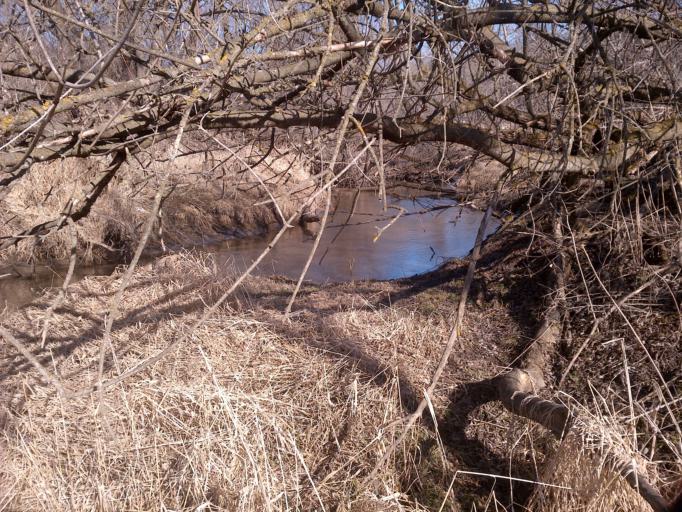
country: US
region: Minnesota
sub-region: Wabasha County
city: Lake City
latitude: 44.4374
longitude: -92.3413
